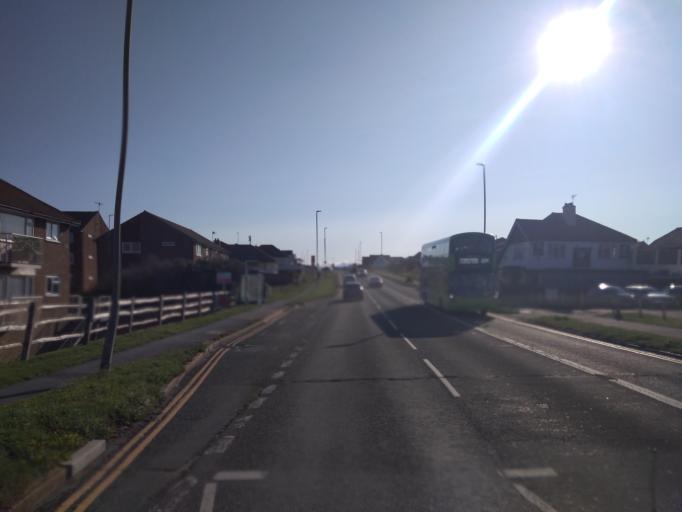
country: GB
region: England
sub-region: East Sussex
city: Peacehaven
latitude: 50.7952
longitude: -0.0197
